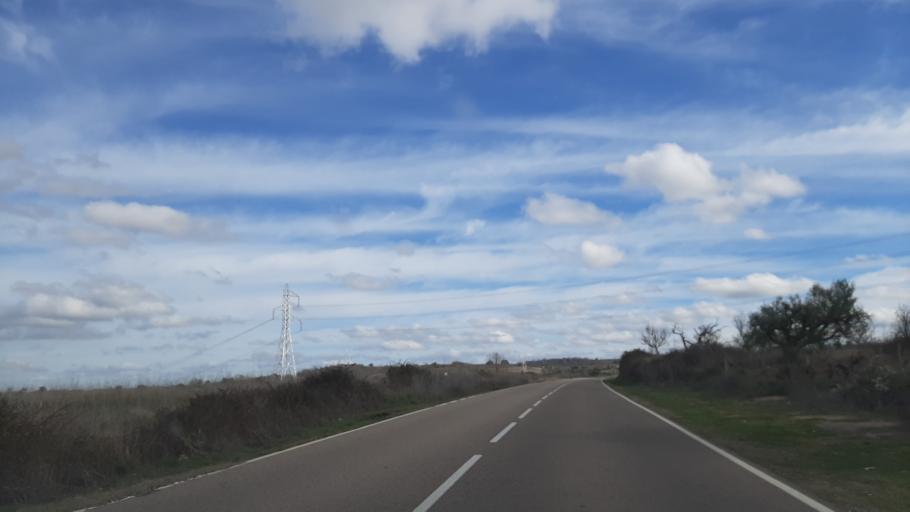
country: ES
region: Castille and Leon
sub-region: Provincia de Salamanca
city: Villarino de los Aires
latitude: 41.2673
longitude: -6.4556
